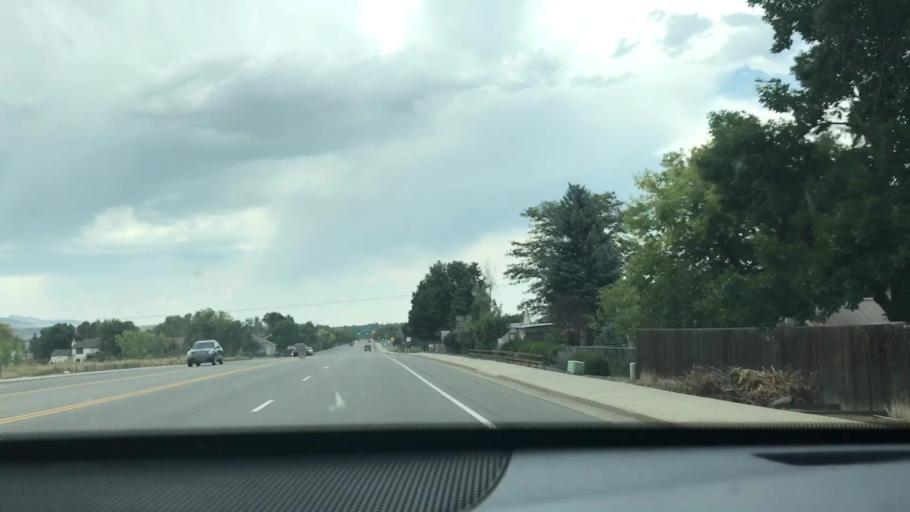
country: US
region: Colorado
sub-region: Larimer County
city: Loveland
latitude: 40.3803
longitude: -105.1158
